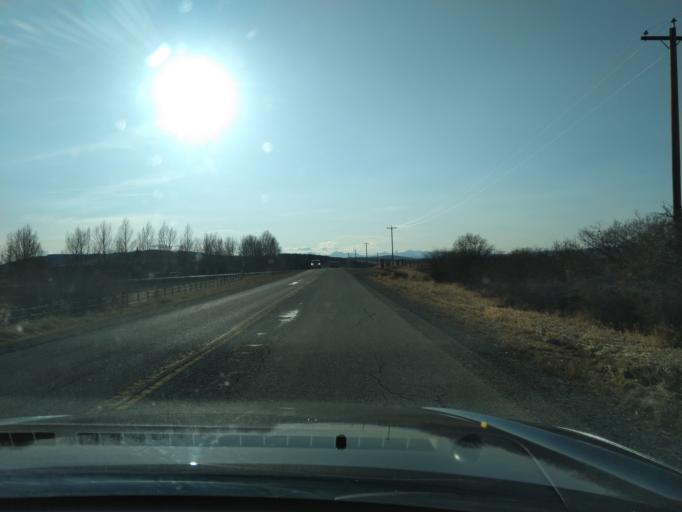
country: CA
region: Alberta
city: Cochrane
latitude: 51.1679
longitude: -114.4846
